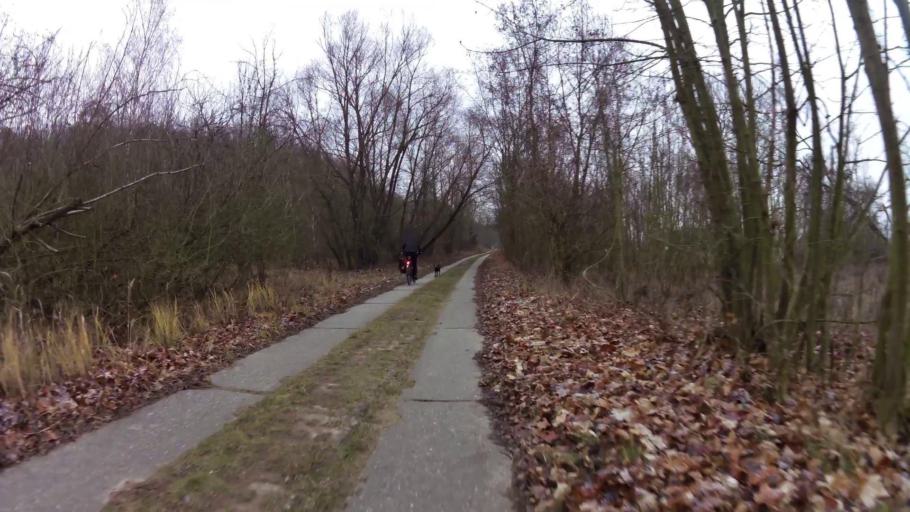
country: PL
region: West Pomeranian Voivodeship
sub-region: Powiat gryfinski
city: Cedynia
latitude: 52.9315
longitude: 14.1505
